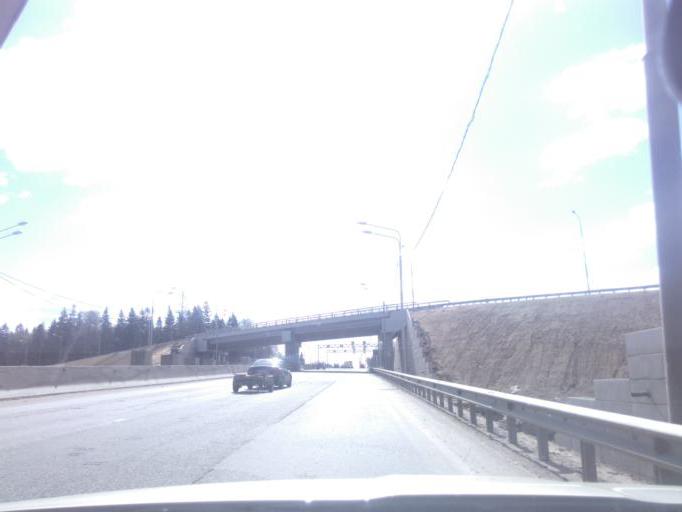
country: RU
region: Moskovskaya
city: Peshki
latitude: 56.1390
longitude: 37.0543
